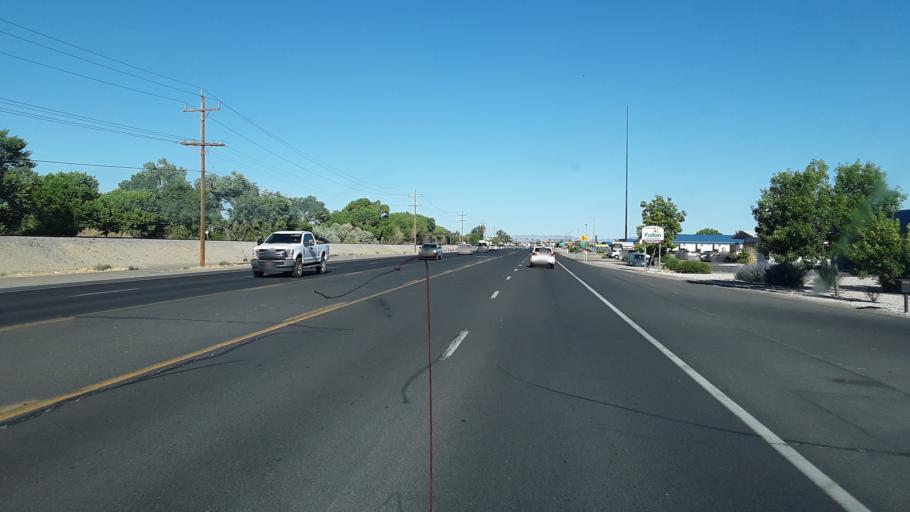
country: US
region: Nevada
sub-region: Churchill County
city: Fallon
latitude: 39.4797
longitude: -118.8144
